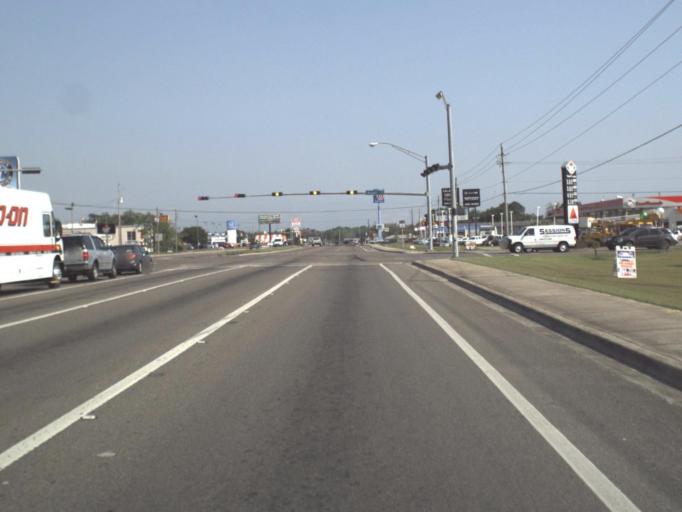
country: US
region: Florida
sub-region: Escambia County
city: Brent
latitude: 30.4747
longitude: -87.2489
